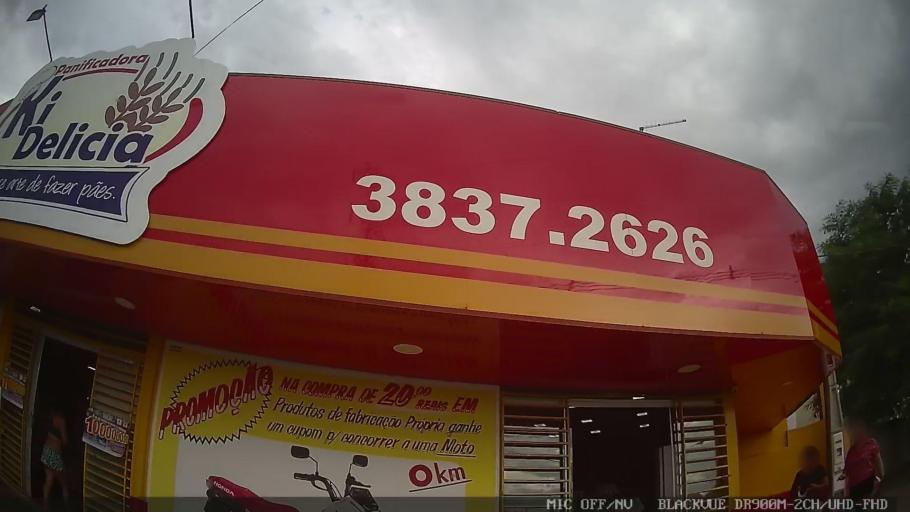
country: BR
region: Sao Paulo
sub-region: Jaguariuna
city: Jaguariuna
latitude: -22.6841
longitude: -46.9819
